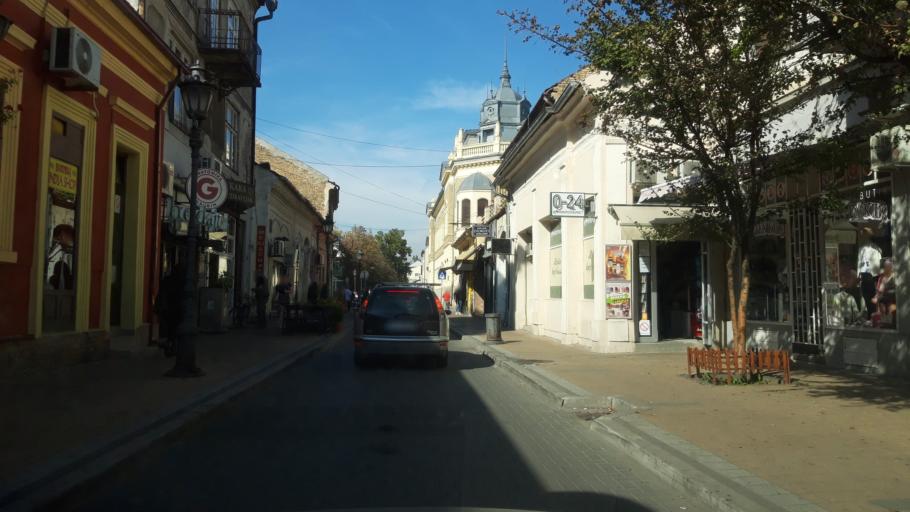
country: RS
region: Autonomna Pokrajina Vojvodina
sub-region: Juznobacki Okrug
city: Novi Sad
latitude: 45.2586
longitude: 19.8457
